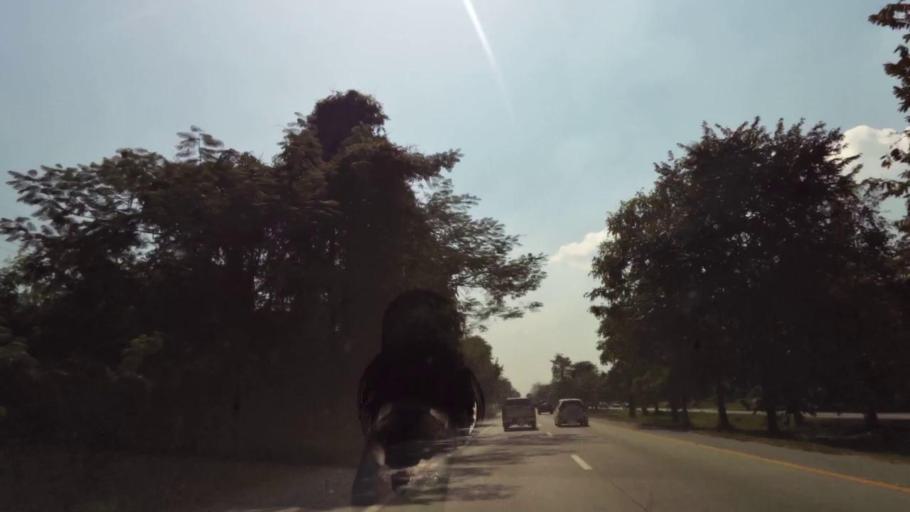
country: TH
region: Phichit
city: Wachira Barami
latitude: 16.5572
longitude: 100.1477
